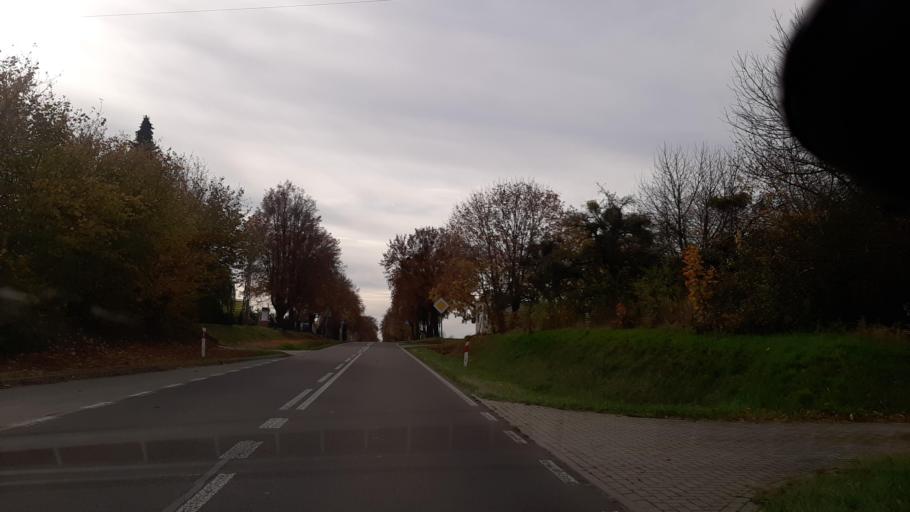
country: PL
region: Lublin Voivodeship
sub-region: Powiat pulawski
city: Markuszow
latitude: 51.3441
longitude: 22.2629
